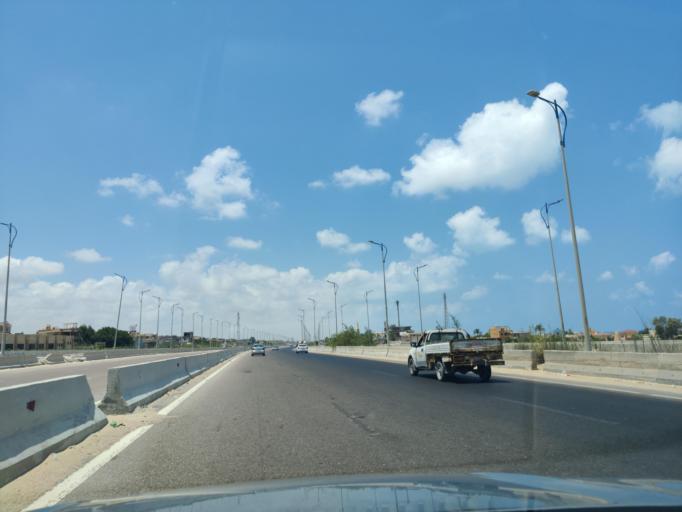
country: EG
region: Alexandria
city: Alexandria
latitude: 30.9704
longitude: 29.5624
